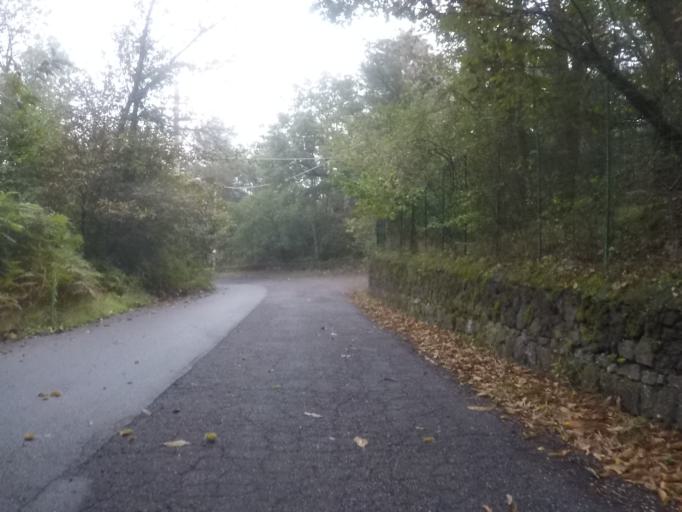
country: IT
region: Sicily
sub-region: Catania
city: Pedara
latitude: 37.6572
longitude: 15.0414
